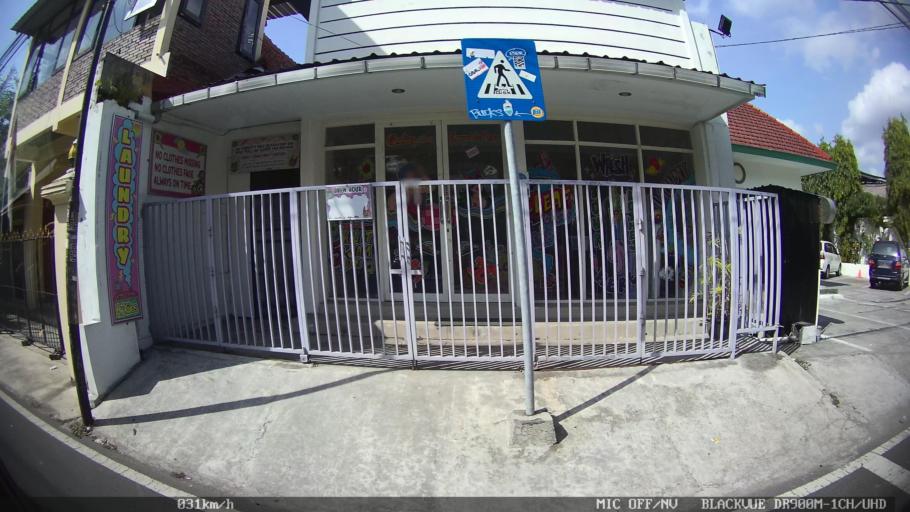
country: ID
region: Daerah Istimewa Yogyakarta
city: Yogyakarta
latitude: -7.8192
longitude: 110.3704
